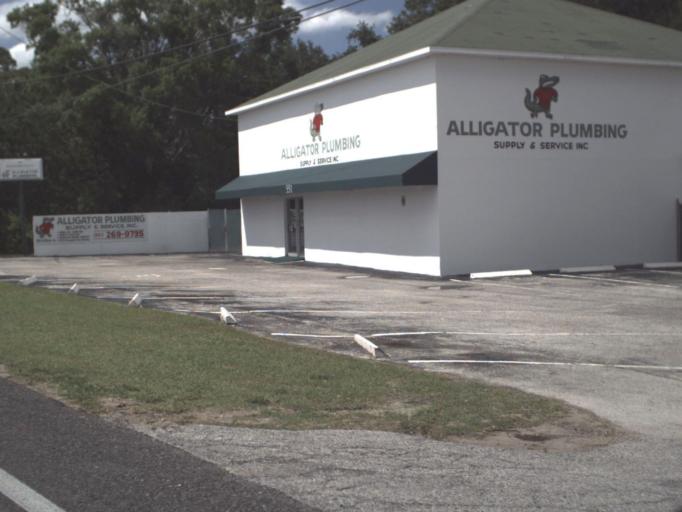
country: US
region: Florida
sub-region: Brevard County
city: Titusville
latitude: 28.6206
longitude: -80.8191
